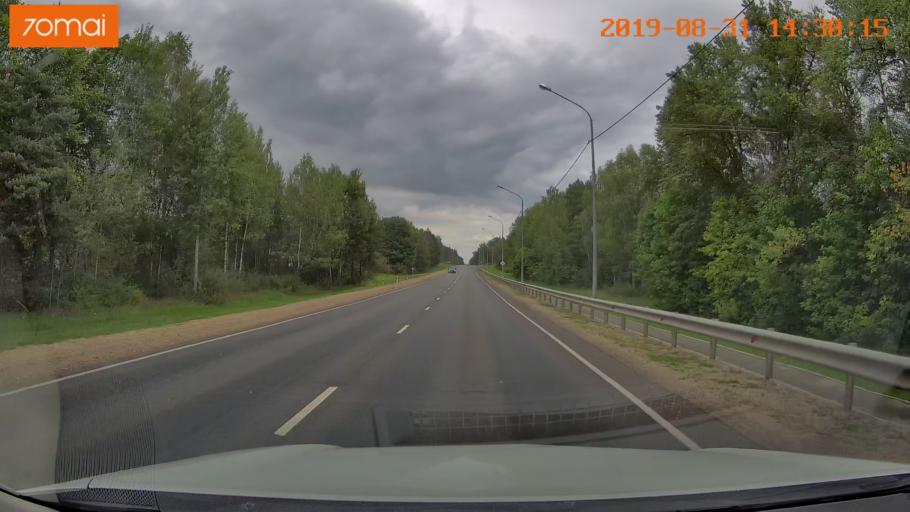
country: RU
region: Smolensk
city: Yekimovichi
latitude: 54.1305
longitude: 33.3473
